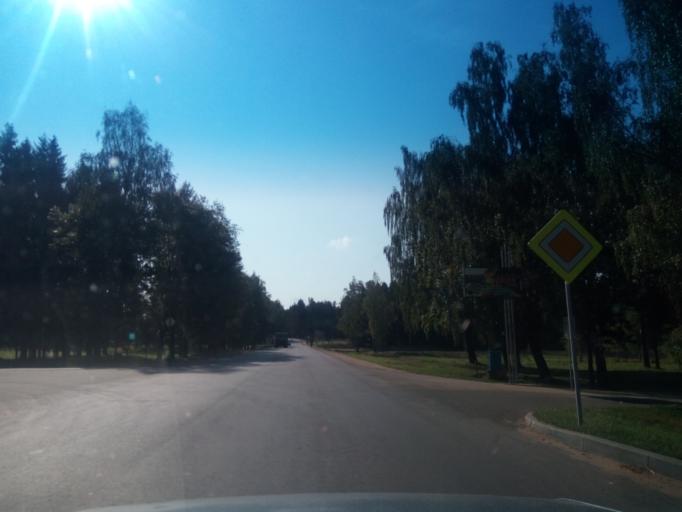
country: BY
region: Vitebsk
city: Vyerkhnyadzvinsk
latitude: 55.7622
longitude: 27.9428
